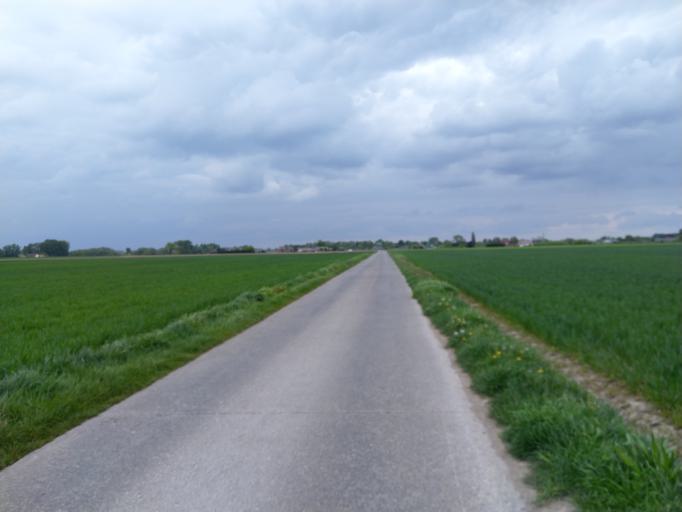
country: BE
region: Wallonia
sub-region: Province du Hainaut
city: Jurbise
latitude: 50.5227
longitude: 3.8984
